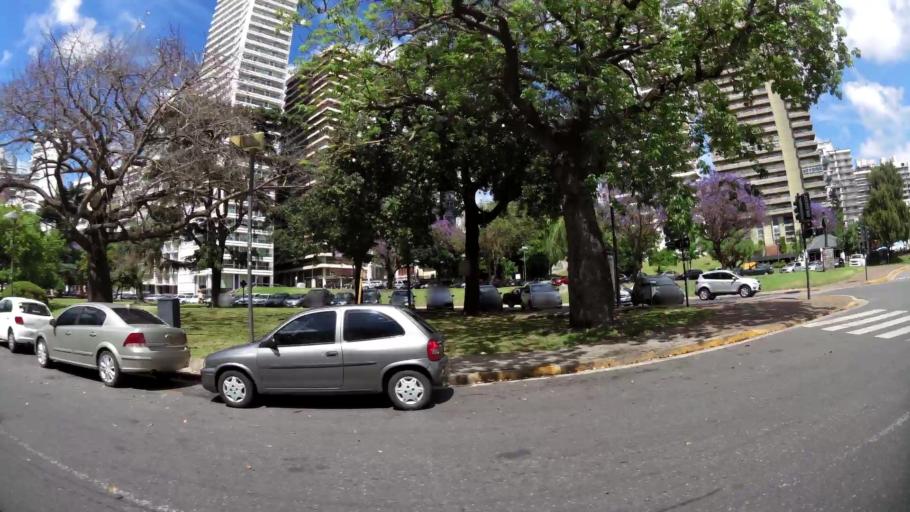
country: AR
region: Santa Fe
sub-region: Departamento de Rosario
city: Rosario
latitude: -32.9501
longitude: -60.6283
